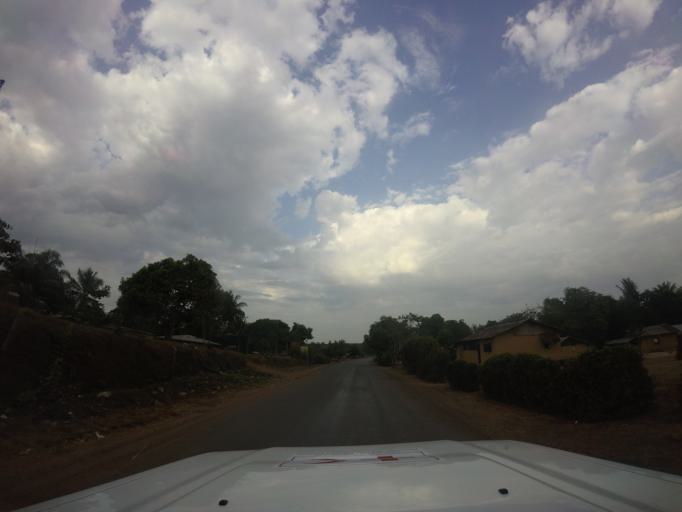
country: LR
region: Bomi
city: Tubmanburg
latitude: 6.7016
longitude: -10.9173
